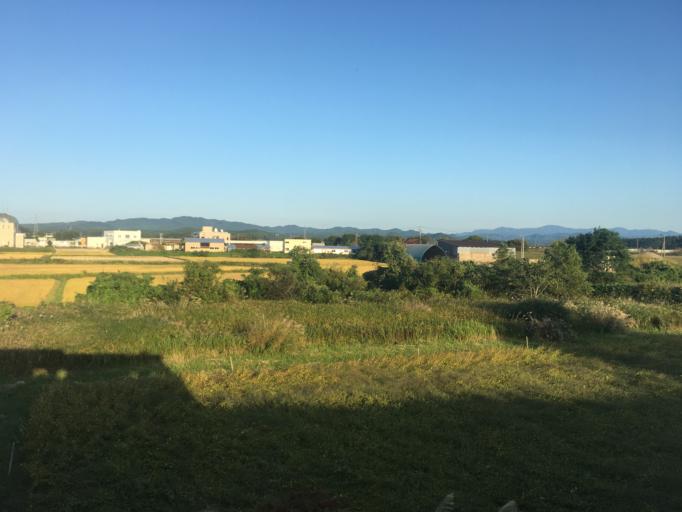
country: JP
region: Akita
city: Takanosu
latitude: 40.2161
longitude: 140.3547
